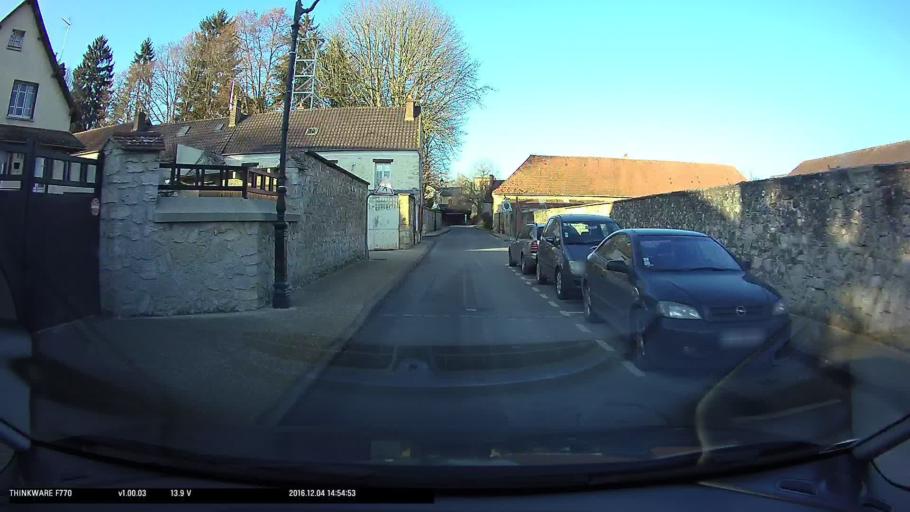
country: FR
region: Ile-de-France
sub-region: Departement du Val-d'Oise
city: Ableiges
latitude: 49.0777
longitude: 2.0036
